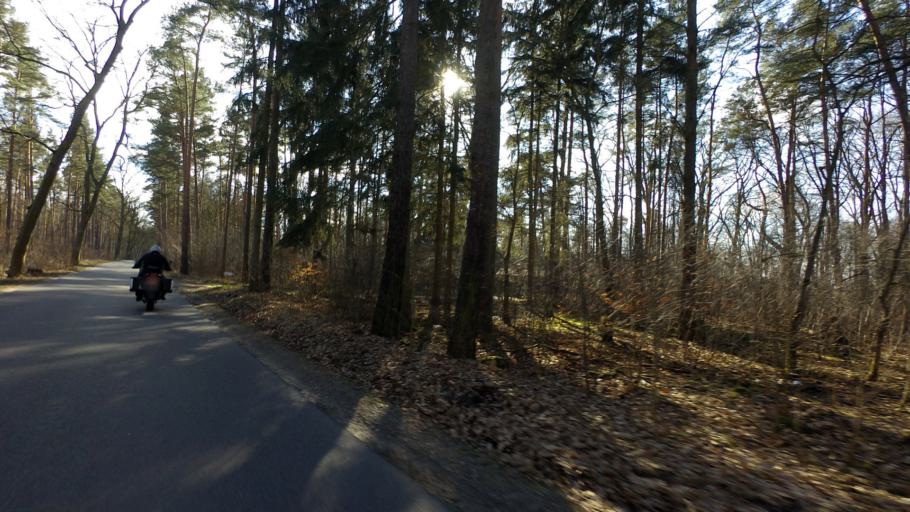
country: DE
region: Brandenburg
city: Oranienburg
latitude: 52.7607
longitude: 13.2825
